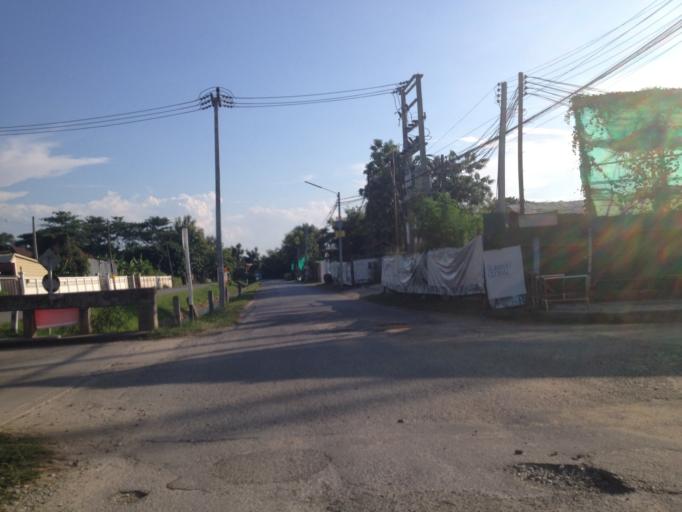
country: TH
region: Chiang Mai
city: Hang Dong
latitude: 18.6975
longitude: 98.9258
